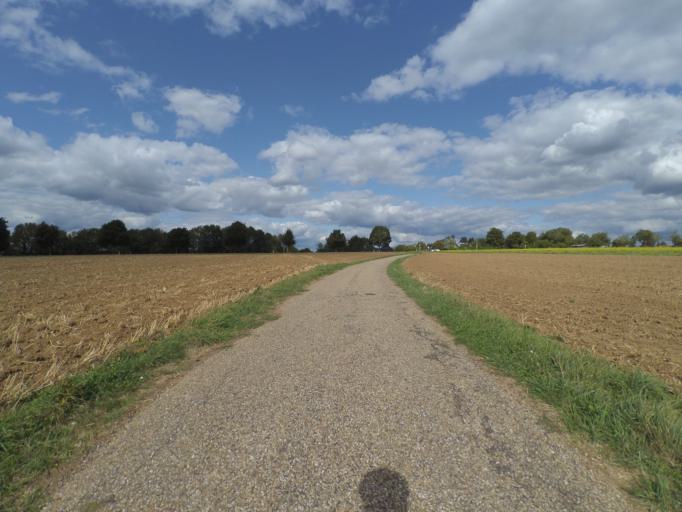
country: LU
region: Grevenmacher
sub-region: Canton de Remich
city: Dalheim
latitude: 49.5382
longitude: 6.2607
